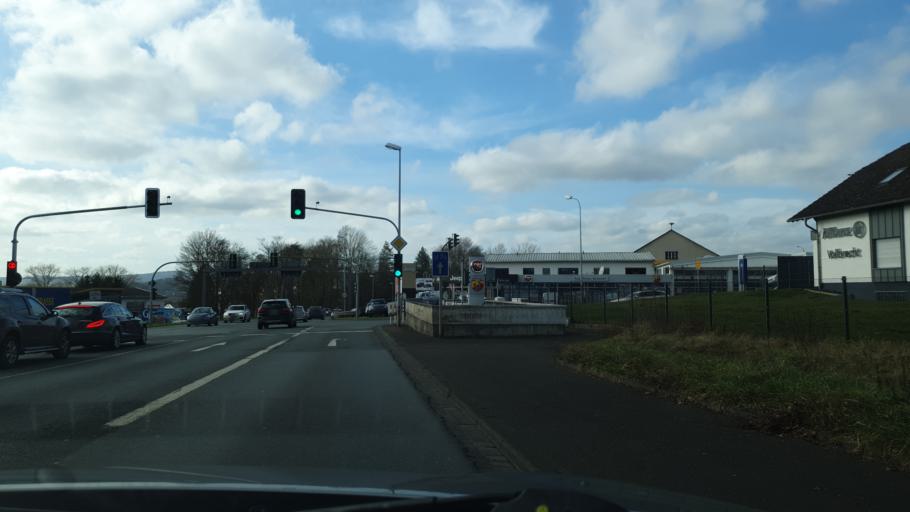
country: DE
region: Hesse
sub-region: Regierungsbezirk Giessen
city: Limburg an der Lahn
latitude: 50.3971
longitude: 8.0637
